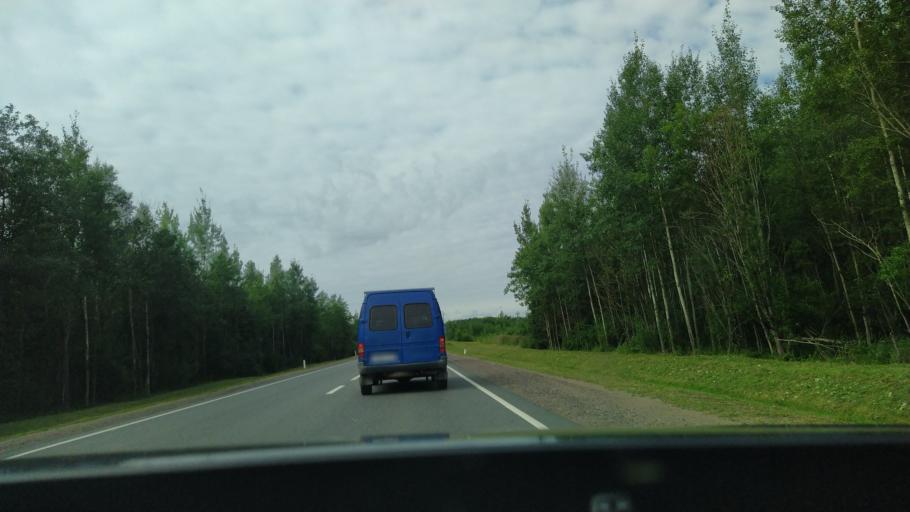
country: RU
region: Leningrad
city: Ul'yanovka
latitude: 59.6092
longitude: 30.7666
